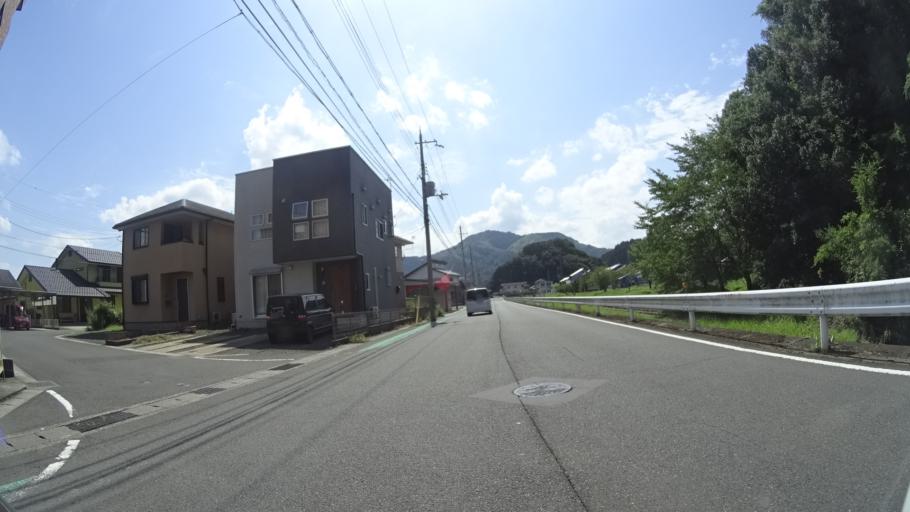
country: JP
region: Kyoto
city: Maizuru
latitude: 35.4326
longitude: 135.3253
